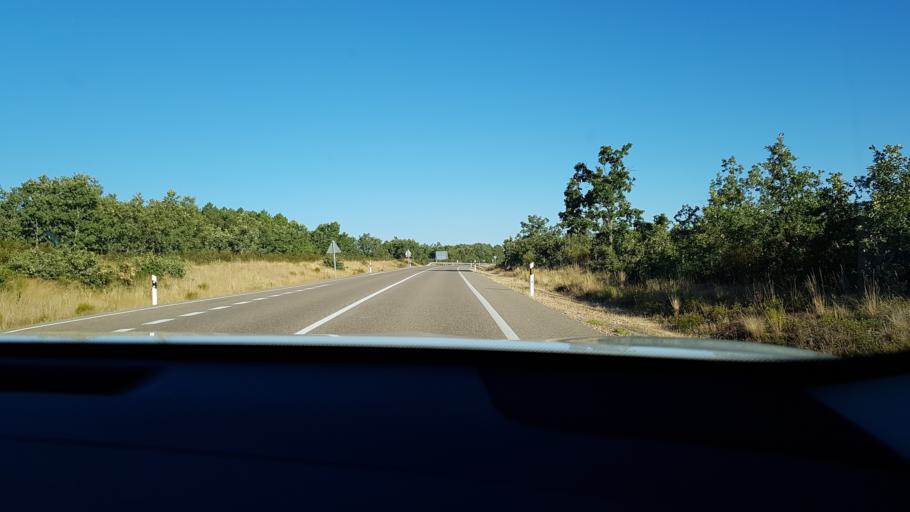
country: ES
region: Castille and Leon
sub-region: Provincia de Zamora
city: Samir de los Canos
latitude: 41.6697
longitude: -6.2283
